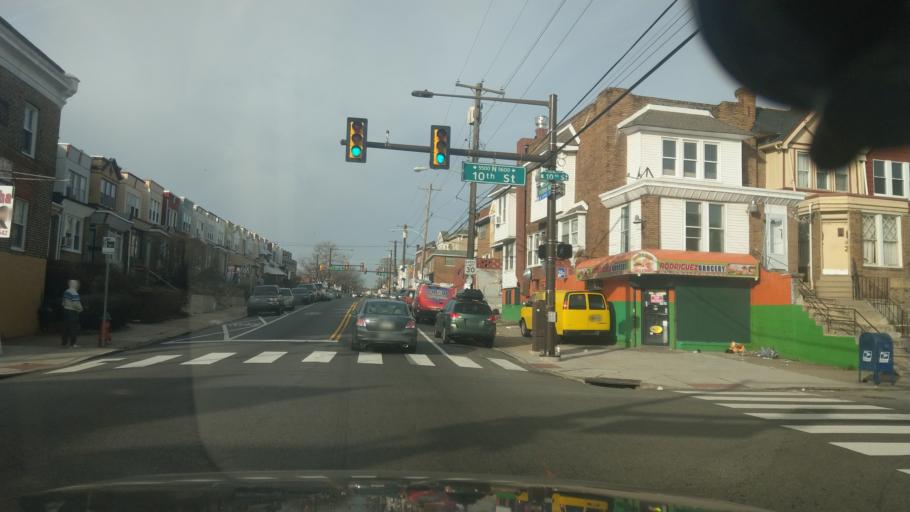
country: US
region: Pennsylvania
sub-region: Montgomery County
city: Wyncote
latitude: 40.0375
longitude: -75.1378
